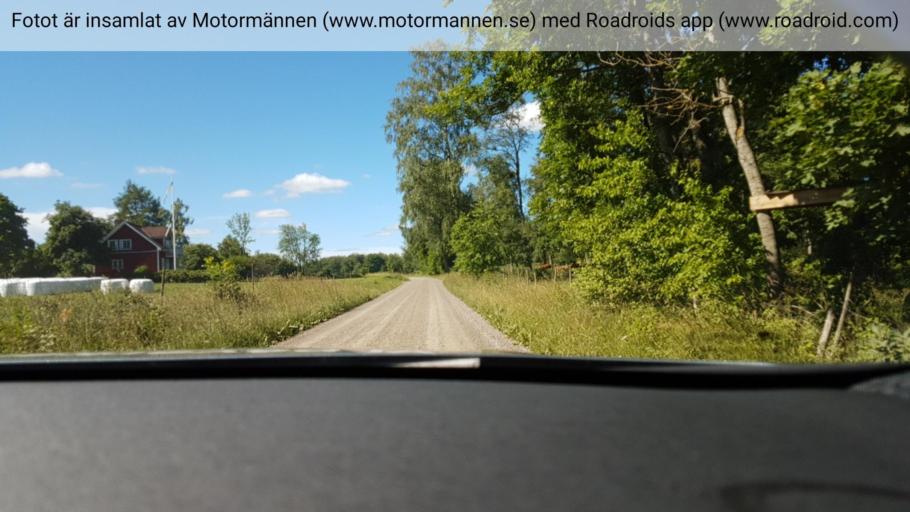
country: SE
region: Vaestra Goetaland
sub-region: Falkopings Kommun
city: Akarp
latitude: 58.2107
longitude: 13.7515
